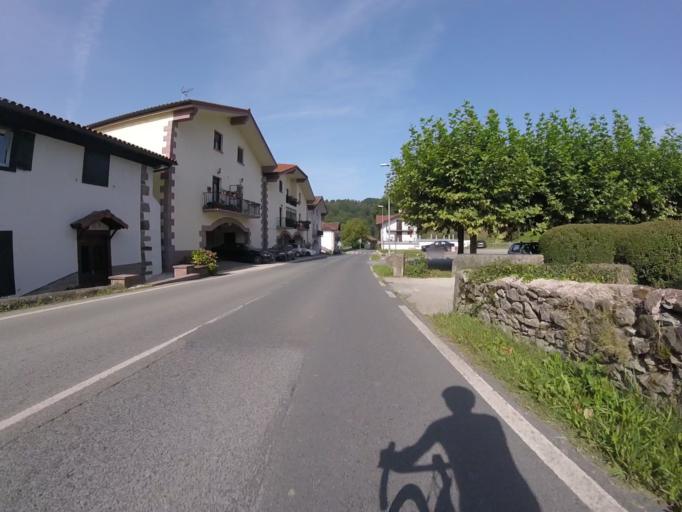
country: ES
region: Navarre
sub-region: Provincia de Navarra
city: Doneztebe
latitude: 43.1309
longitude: -1.5487
